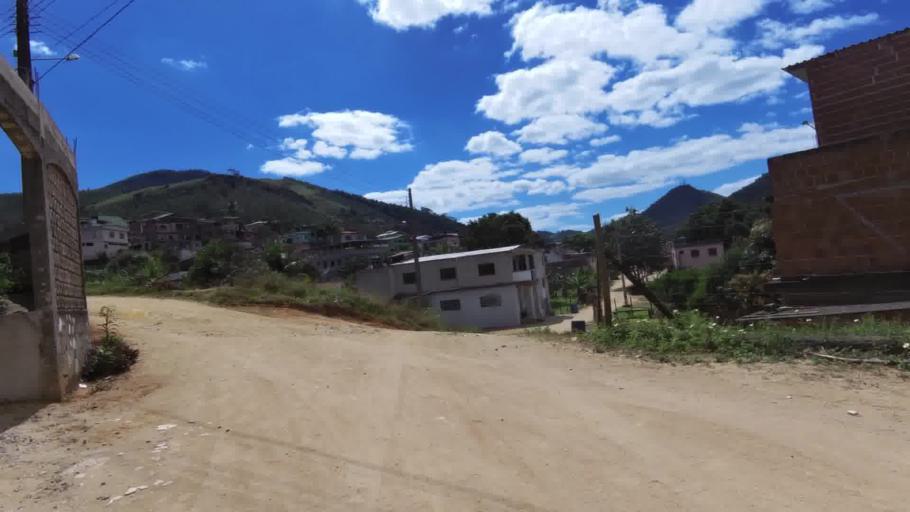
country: BR
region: Espirito Santo
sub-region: Rio Novo Do Sul
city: Rio Novo do Sul
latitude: -20.8685
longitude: -40.9424
